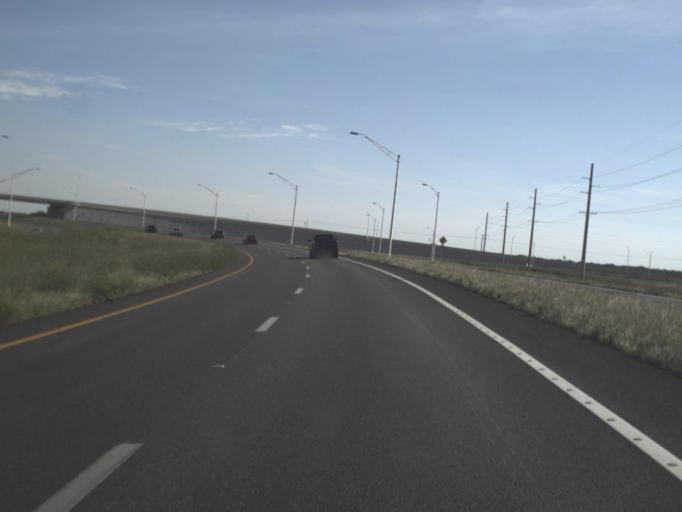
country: US
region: Florida
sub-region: Glades County
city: Moore Haven
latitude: 26.7581
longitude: -81.0832
